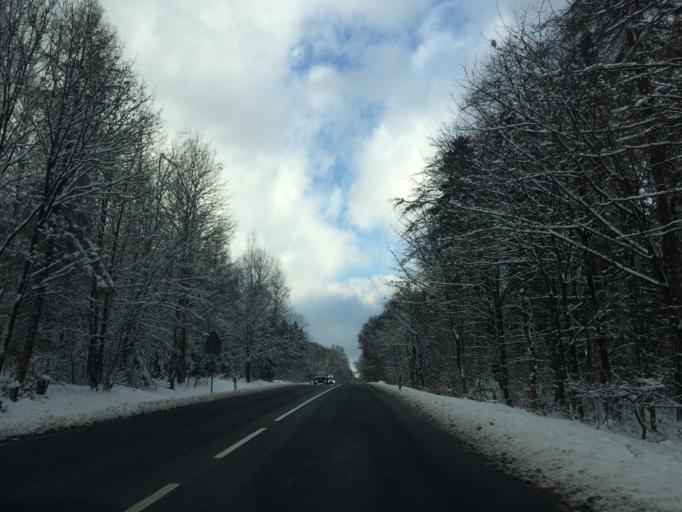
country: DE
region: Hesse
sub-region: Regierungsbezirk Darmstadt
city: Glashutten
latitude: 50.2071
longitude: 8.4321
